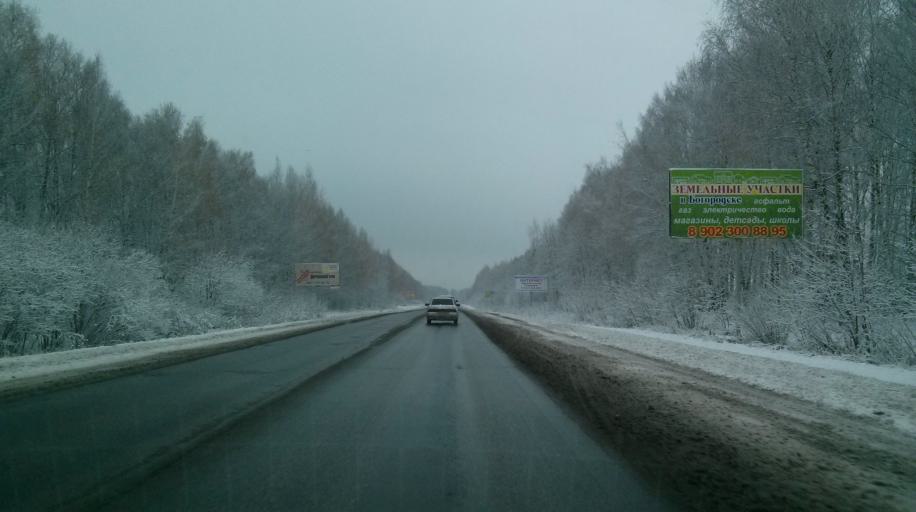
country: RU
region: Nizjnij Novgorod
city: Burevestnik
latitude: 56.1545
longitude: 43.7019
